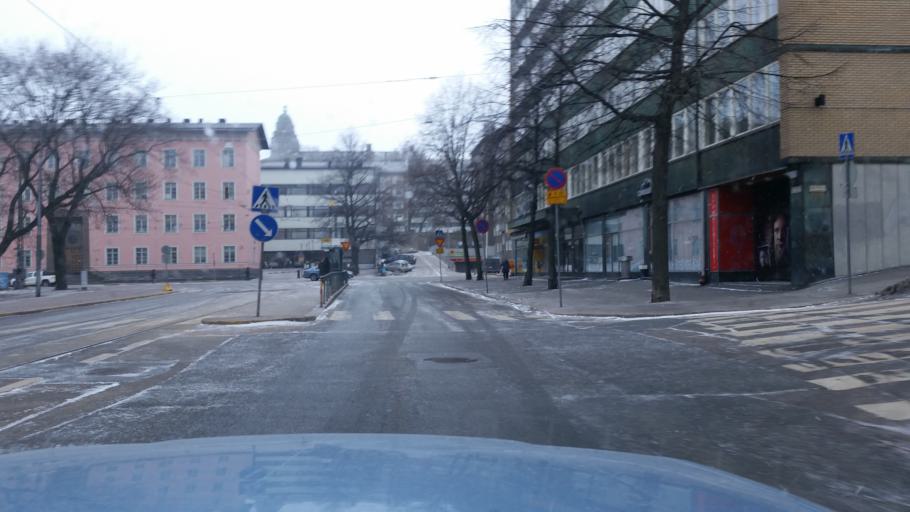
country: FI
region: Uusimaa
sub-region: Helsinki
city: Helsinki
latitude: 60.1872
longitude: 24.9483
